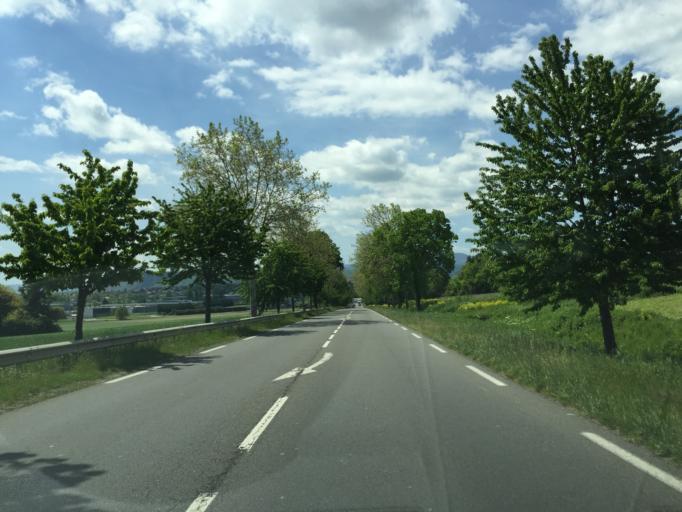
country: FR
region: Auvergne
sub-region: Departement du Puy-de-Dome
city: Riom
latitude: 45.9133
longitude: 3.1315
